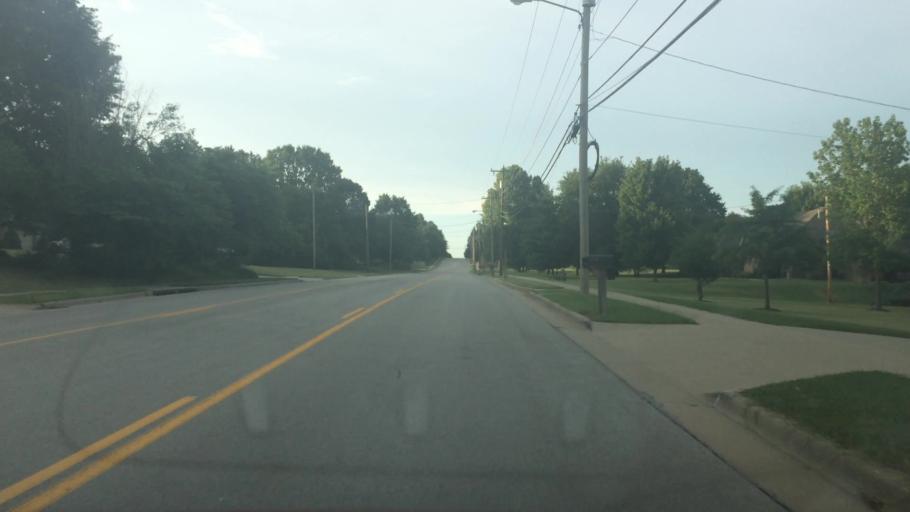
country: US
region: Missouri
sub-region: Greene County
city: Strafford
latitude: 37.1988
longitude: -93.1890
